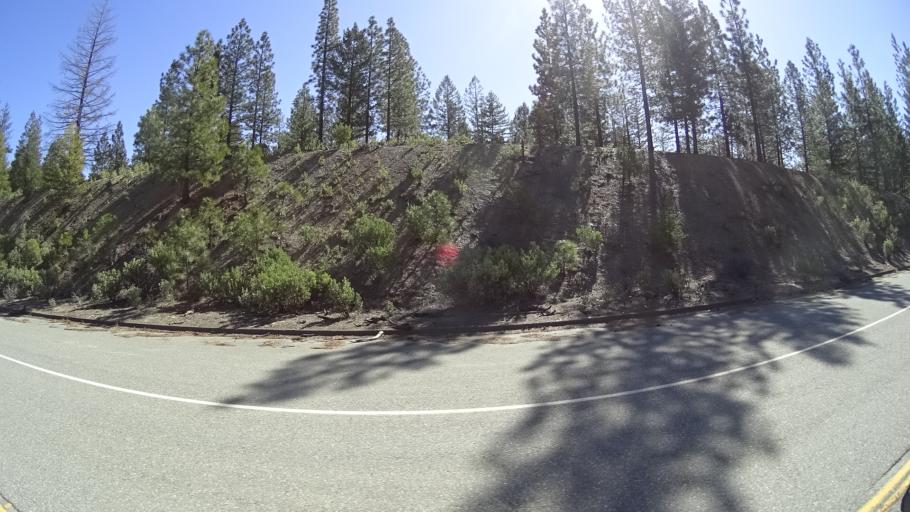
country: US
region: California
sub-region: Tehama County
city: Rancho Tehama Reserve
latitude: 39.6479
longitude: -122.7419
